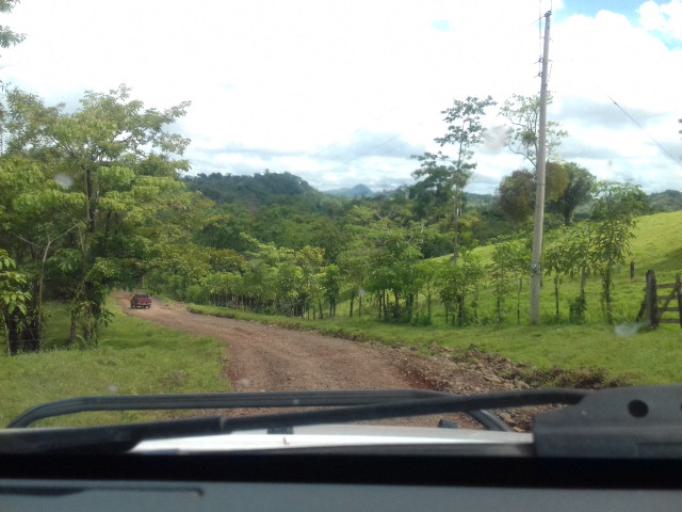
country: NI
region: Matagalpa
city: Rio Blanco
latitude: 13.0008
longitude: -85.1991
